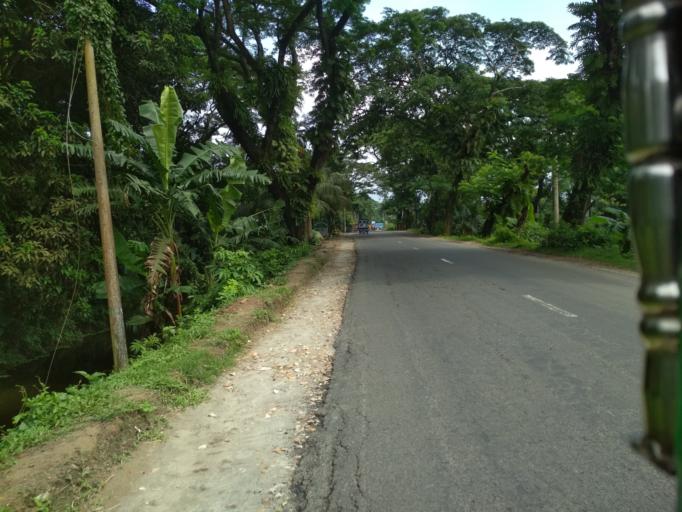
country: BD
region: Chittagong
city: Lakshmipur
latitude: 22.9644
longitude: 90.8097
